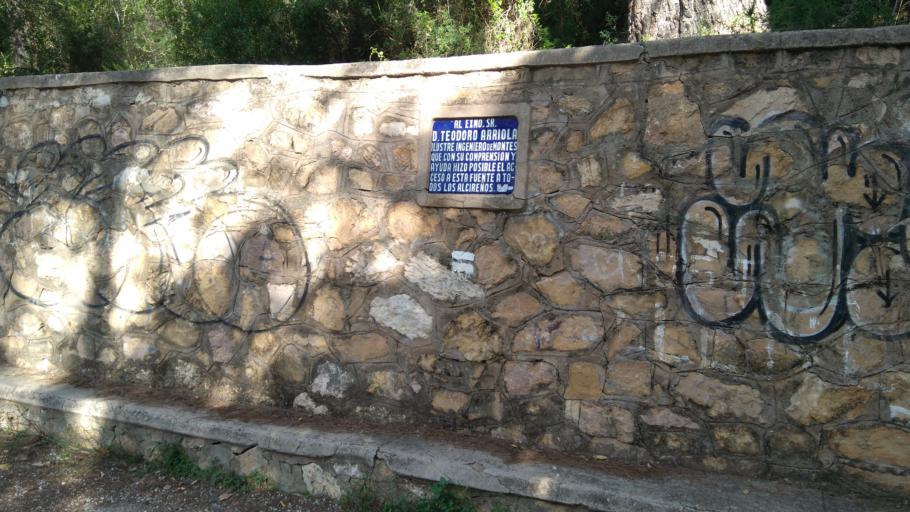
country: ES
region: Valencia
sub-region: Provincia de Valencia
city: Llauri
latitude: 39.1065
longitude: -0.3272
